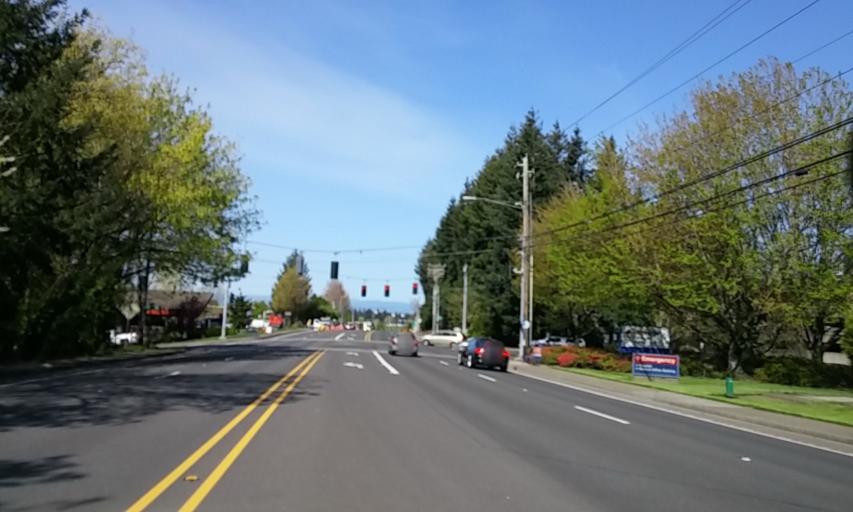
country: US
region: Oregon
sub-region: Washington County
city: West Haven-Sylvan
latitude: 45.5088
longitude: -122.7697
